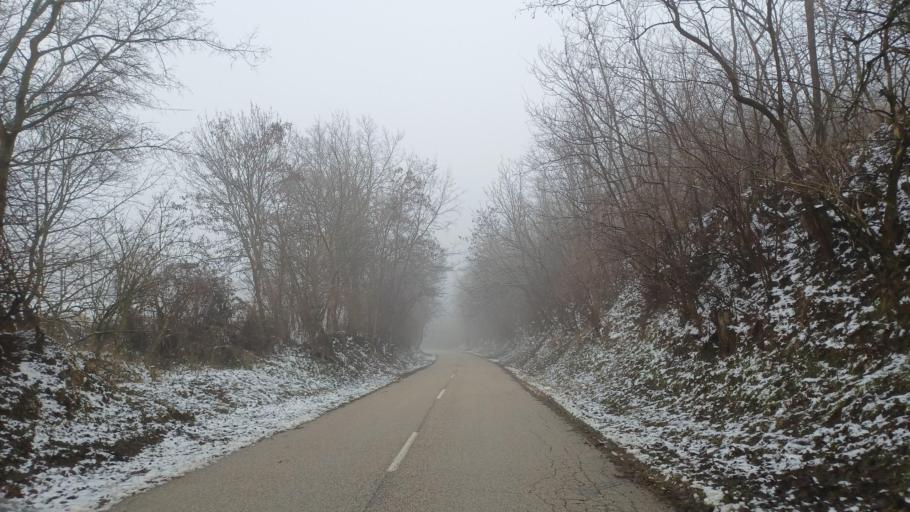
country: HU
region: Tolna
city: Gyonk
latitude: 46.6228
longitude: 18.4803
